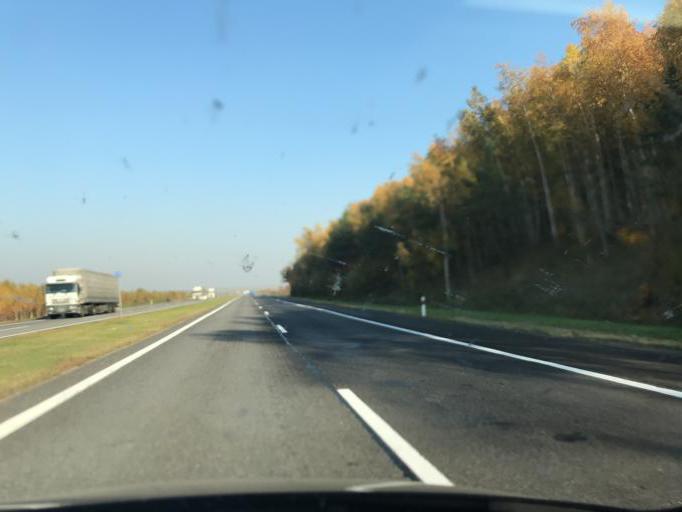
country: BY
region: Minsk
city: Snow
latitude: 53.2454
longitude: 26.2054
